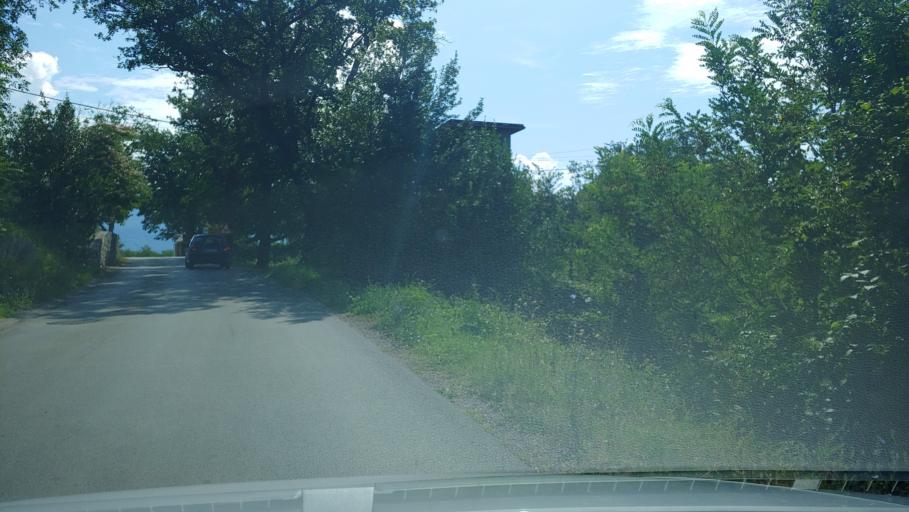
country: SI
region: Ajdovscina
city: Lokavec
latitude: 45.8784
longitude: 13.8660
